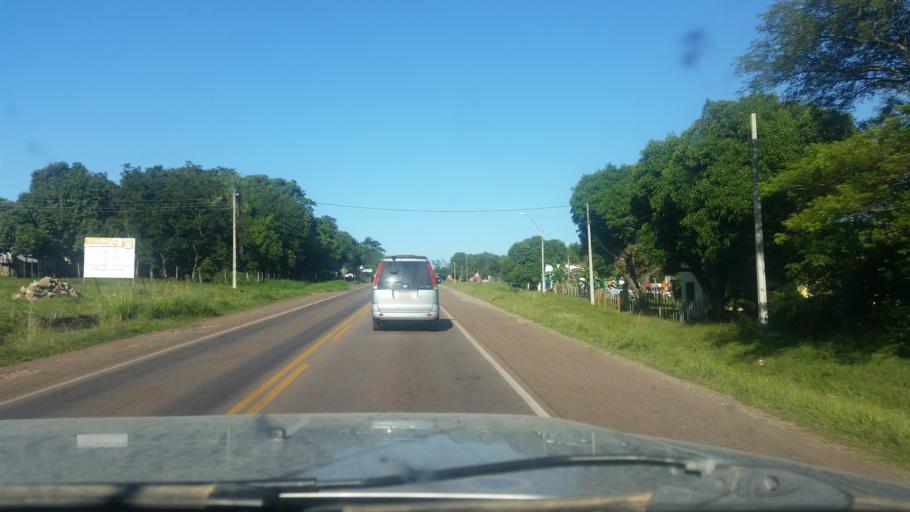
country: PY
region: Paraguari
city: Sapucai
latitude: -25.6640
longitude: -56.9656
